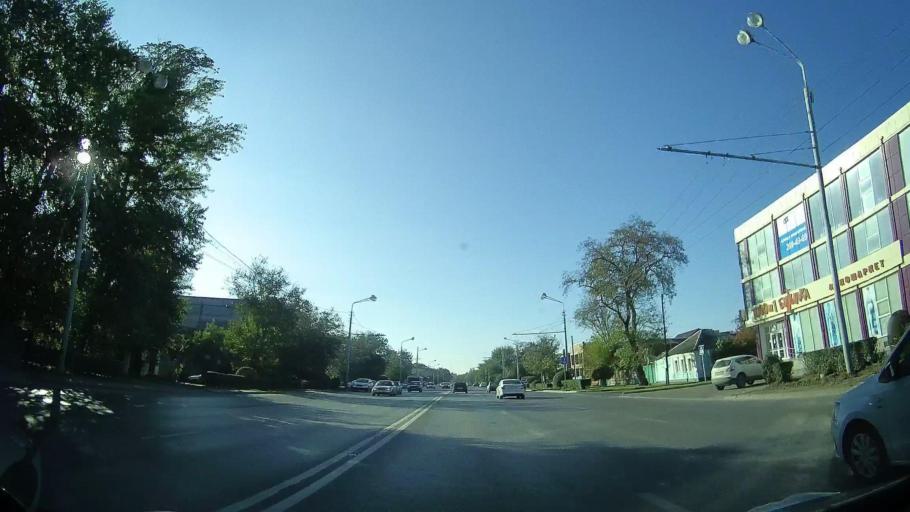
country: RU
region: Rostov
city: Rostov-na-Donu
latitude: 47.2118
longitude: 39.6554
